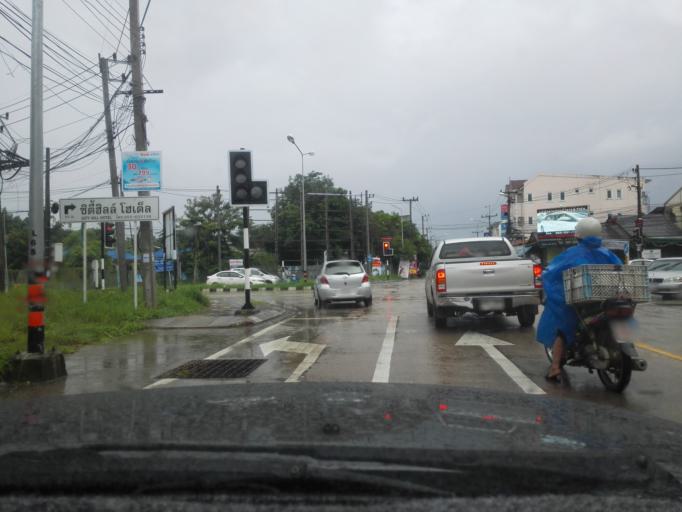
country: TH
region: Tak
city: Mae Sot
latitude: 16.7182
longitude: 98.5850
